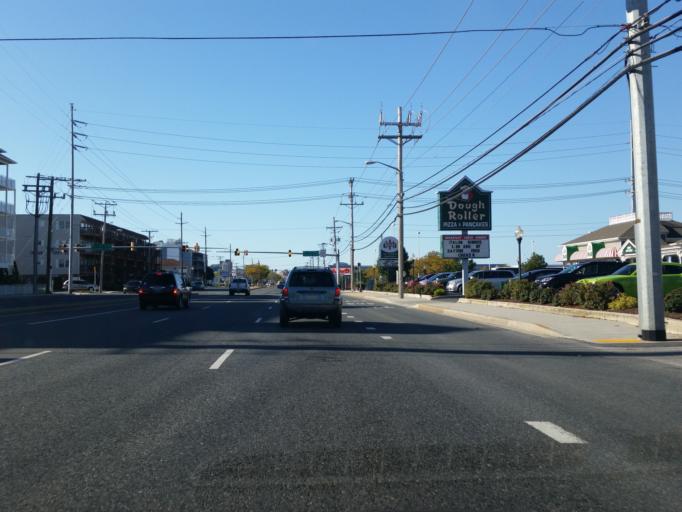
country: US
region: Maryland
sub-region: Worcester County
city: Ocean City
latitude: 38.3689
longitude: -75.0712
